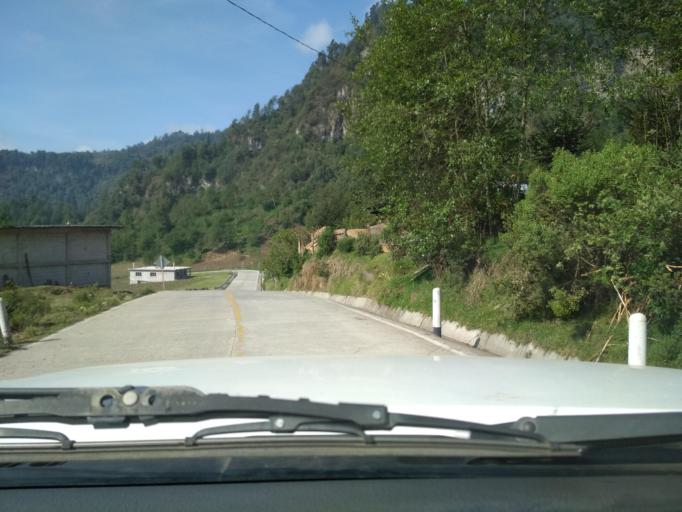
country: MX
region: Veracruz
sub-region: La Perla
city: Chilapa
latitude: 18.9989
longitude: -97.1862
